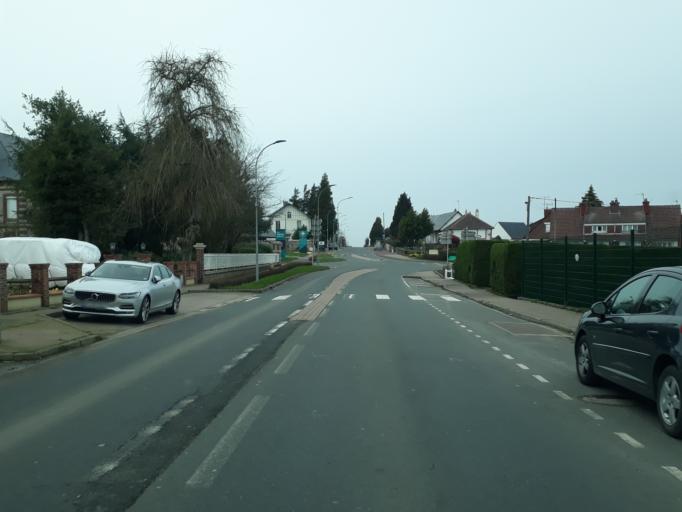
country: FR
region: Haute-Normandie
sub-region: Departement de la Seine-Maritime
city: Breaute
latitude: 49.6270
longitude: 0.3985
